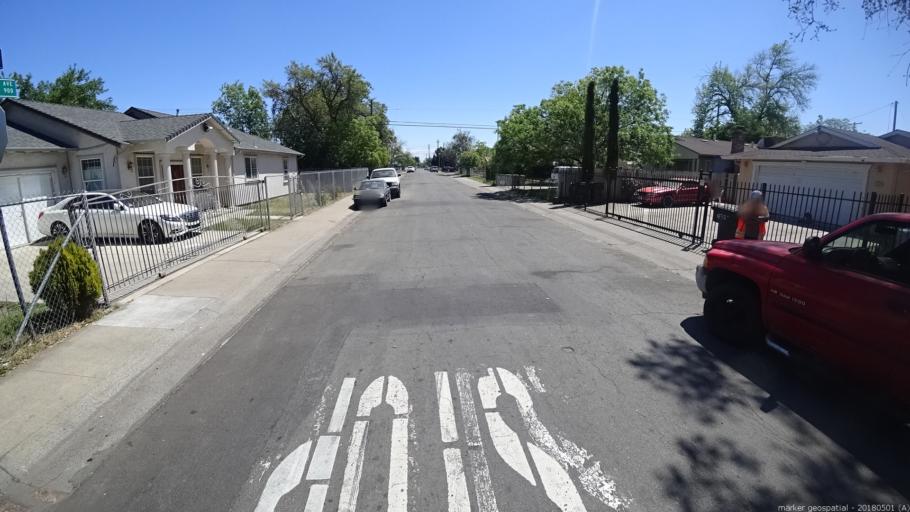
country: US
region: California
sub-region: Sacramento County
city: Rio Linda
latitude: 38.6349
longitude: -121.4449
